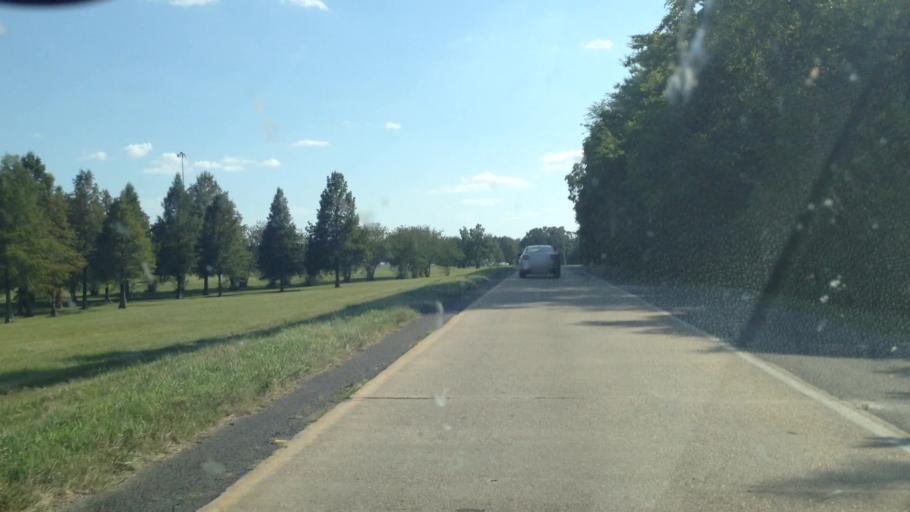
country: US
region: Louisiana
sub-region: Lafayette Parish
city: Lafayette
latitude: 30.2623
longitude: -92.0173
